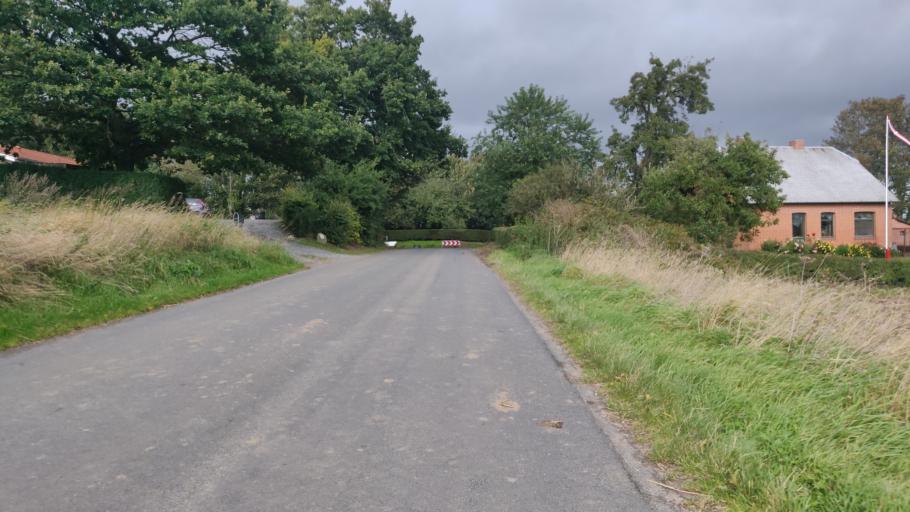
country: DK
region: South Denmark
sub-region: Kolding Kommune
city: Lunderskov
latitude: 55.5355
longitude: 9.3796
